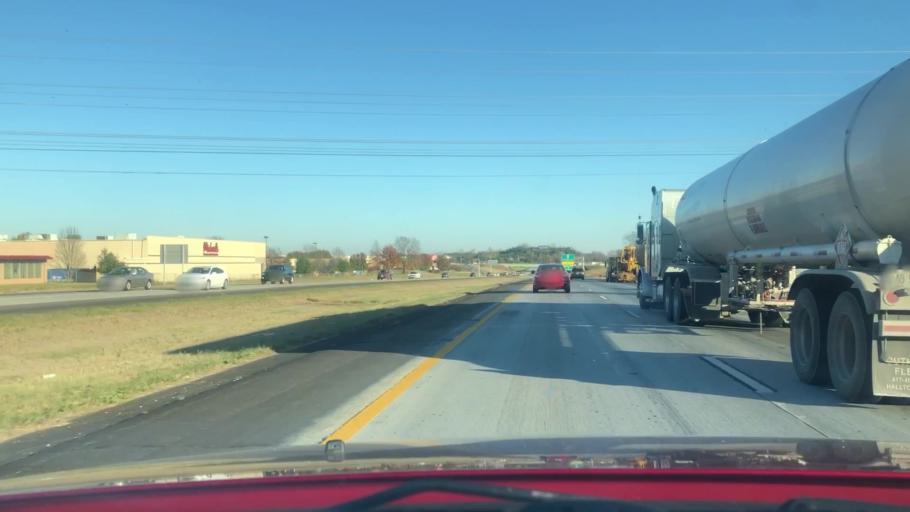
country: US
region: Missouri
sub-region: Greene County
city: Springfield
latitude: 37.1411
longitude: -93.2631
